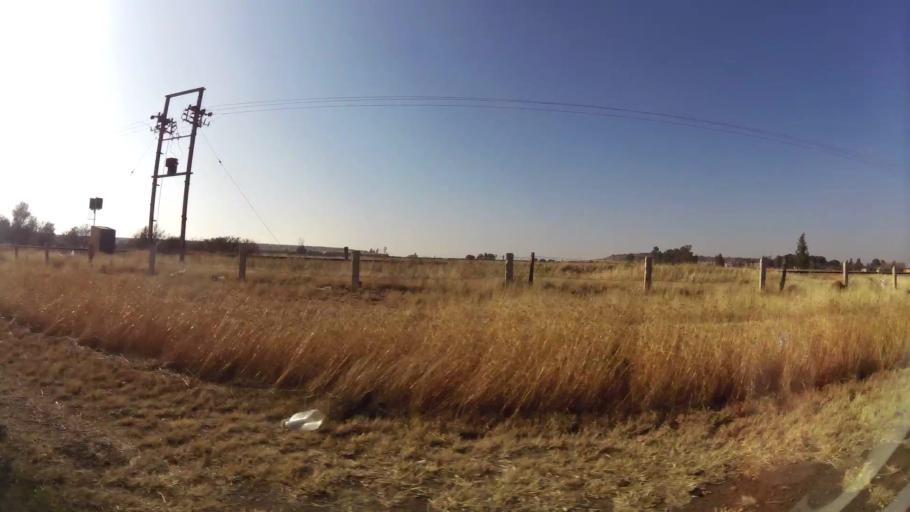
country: ZA
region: Orange Free State
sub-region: Mangaung Metropolitan Municipality
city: Bloemfontein
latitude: -29.1852
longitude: 26.1868
